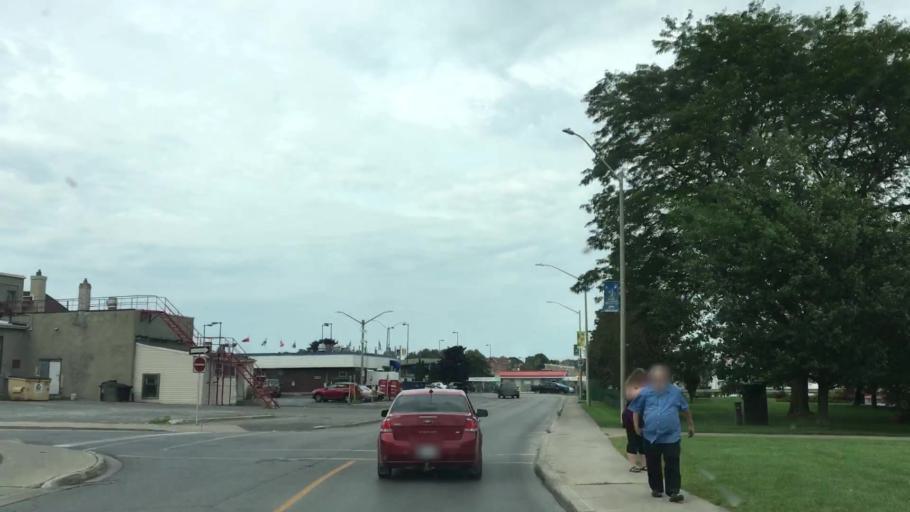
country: CA
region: Ontario
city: Quinte West
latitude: 44.1005
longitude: -77.5757
